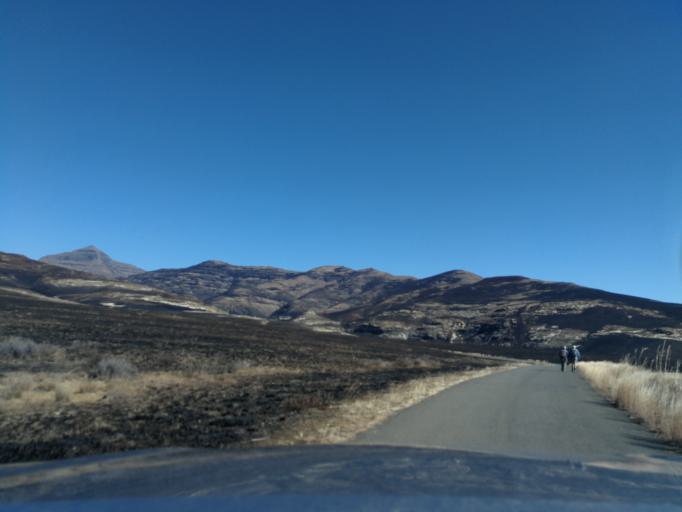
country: ZA
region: Orange Free State
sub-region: Thabo Mofutsanyana District Municipality
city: Phuthaditjhaba
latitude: -28.5125
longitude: 28.6228
